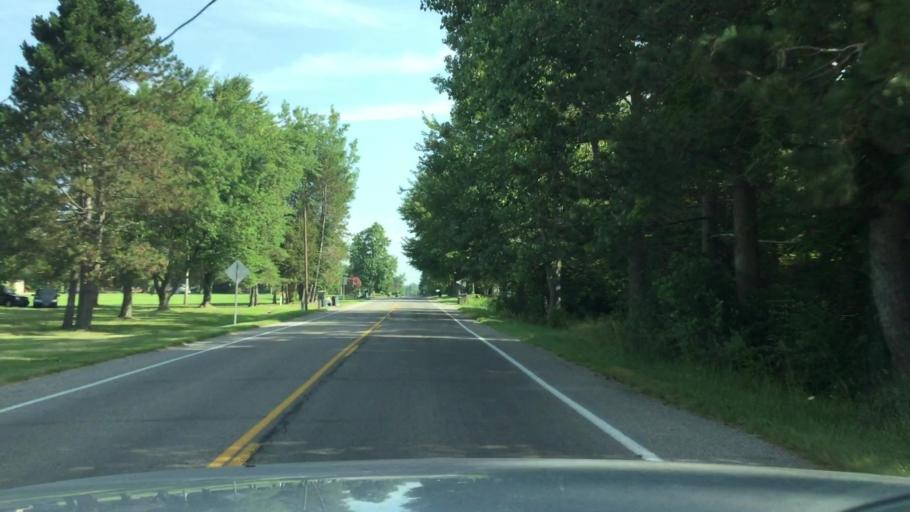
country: US
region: Michigan
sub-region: Genesee County
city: Flushing
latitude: 43.1098
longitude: -83.8728
